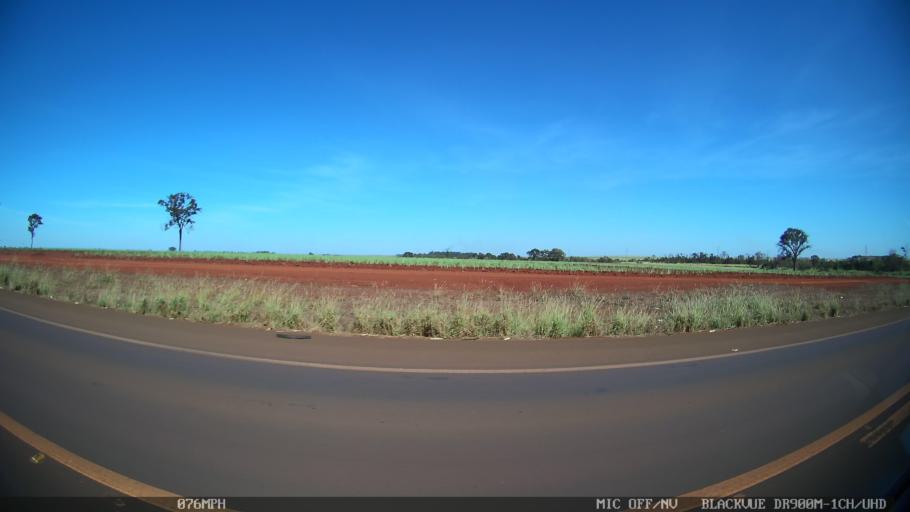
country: BR
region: Sao Paulo
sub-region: Guaira
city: Guaira
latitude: -20.4457
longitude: -48.4102
